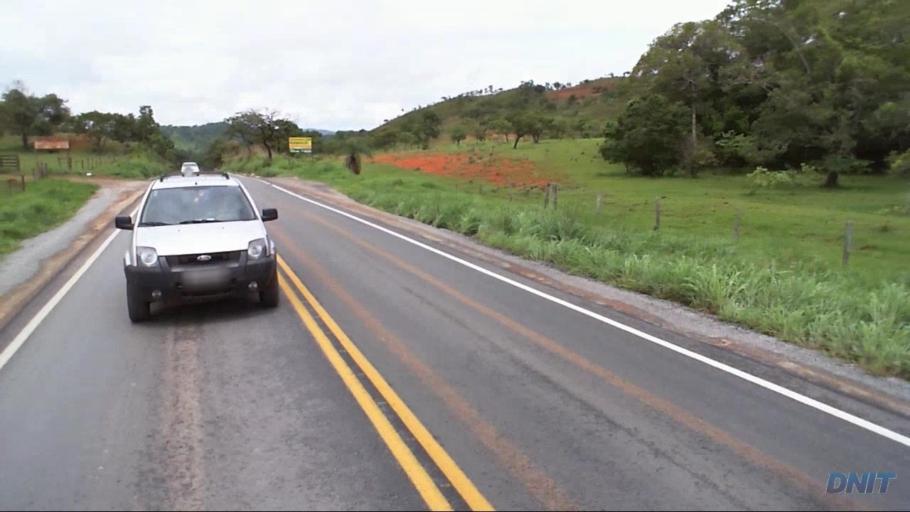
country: BR
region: Goias
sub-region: Padre Bernardo
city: Padre Bernardo
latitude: -15.5035
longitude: -48.2058
